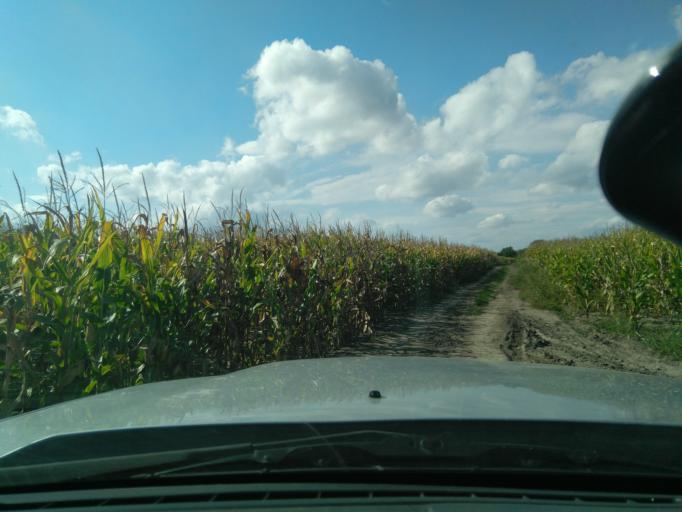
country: HU
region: Fejer
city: Bicske
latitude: 47.4823
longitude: 18.6587
